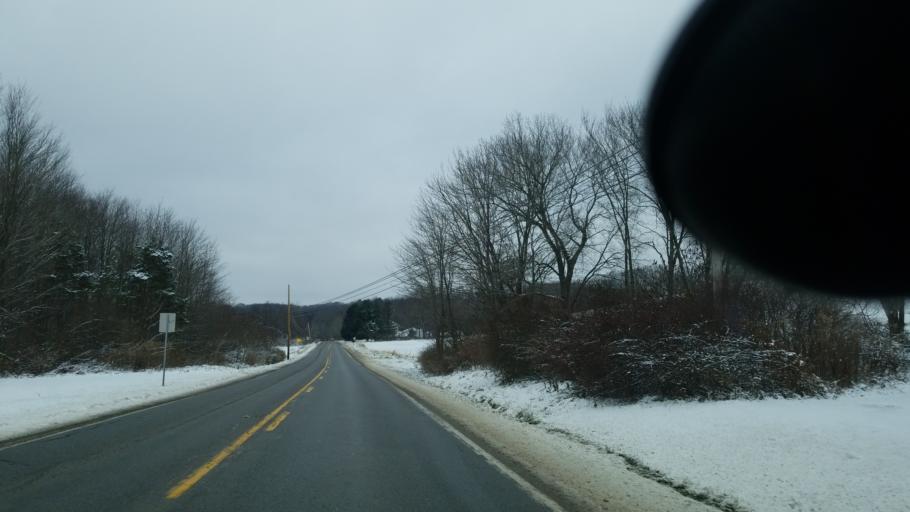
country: US
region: Pennsylvania
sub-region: Indiana County
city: Johnsonburg
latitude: 40.9291
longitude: -78.8983
